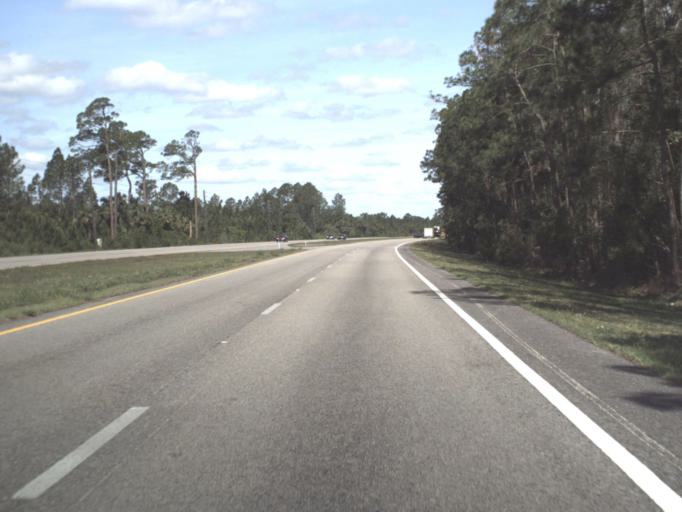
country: US
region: Florida
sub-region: Volusia County
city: Ormond-by-the-Sea
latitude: 29.3626
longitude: -81.1671
